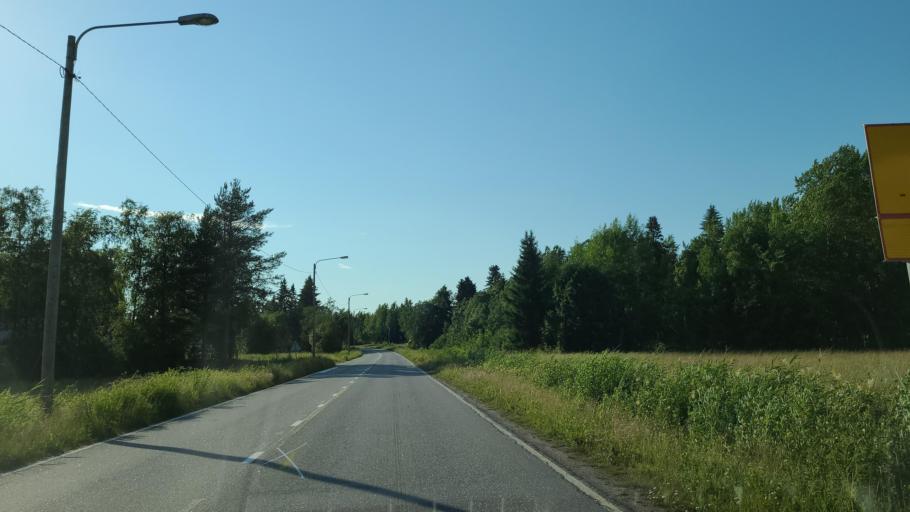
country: FI
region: Ostrobothnia
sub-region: Vaasa
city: Replot
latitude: 63.2335
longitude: 21.4057
